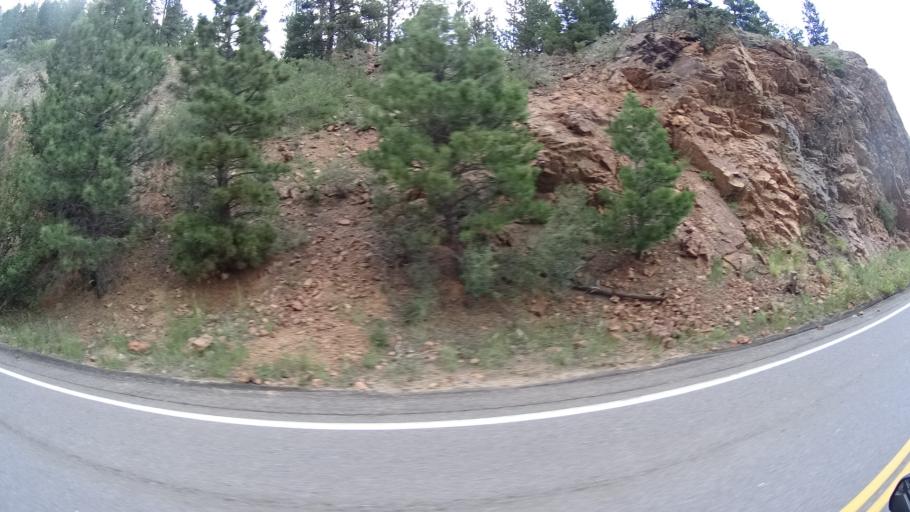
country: US
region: Colorado
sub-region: El Paso County
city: Cascade-Chipita Park
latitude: 38.8965
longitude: -104.9837
